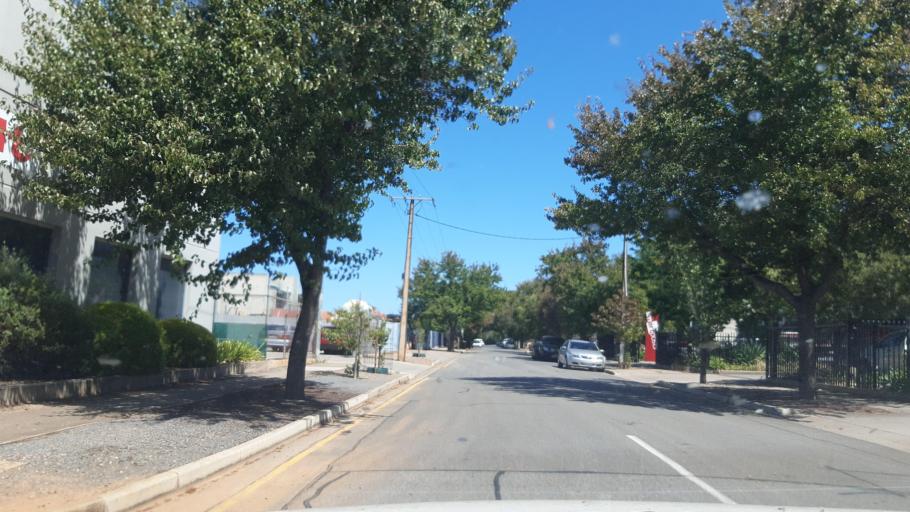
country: AU
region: South Australia
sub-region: Marion
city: Clovelly Park
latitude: -34.9857
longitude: 138.5704
